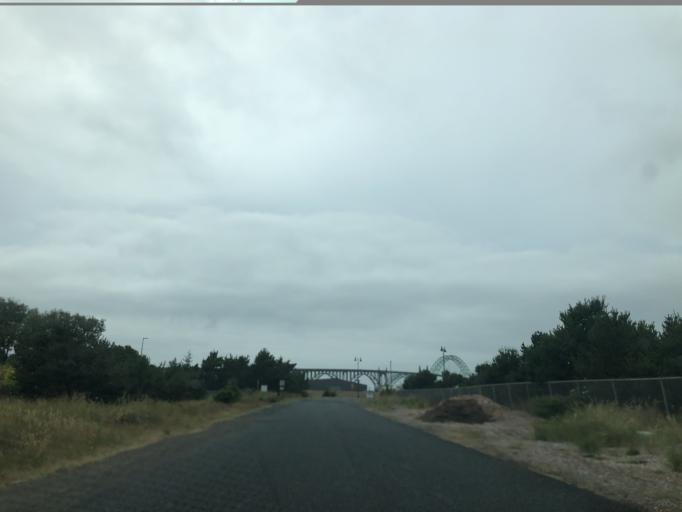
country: US
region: Oregon
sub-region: Lincoln County
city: Newport
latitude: 44.6196
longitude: -124.0466
